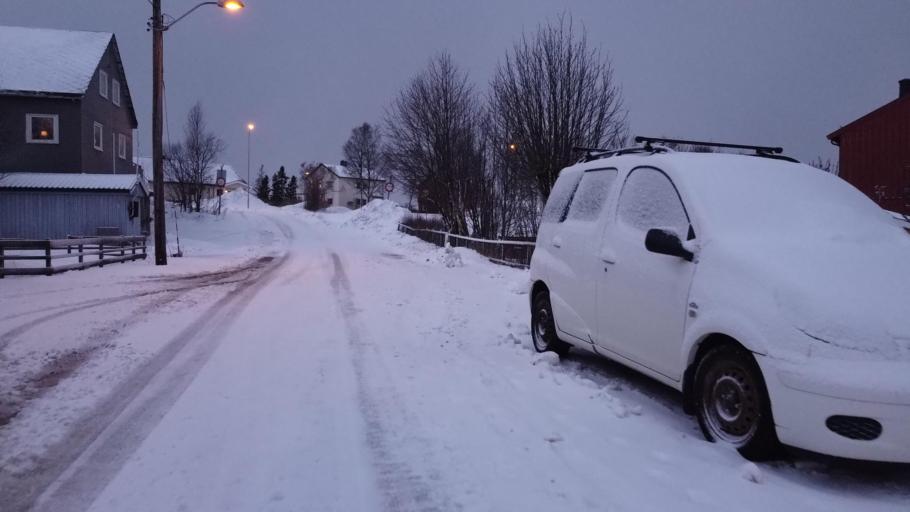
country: NO
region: Nordland
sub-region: Rana
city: Mo i Rana
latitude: 66.3158
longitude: 14.1581
